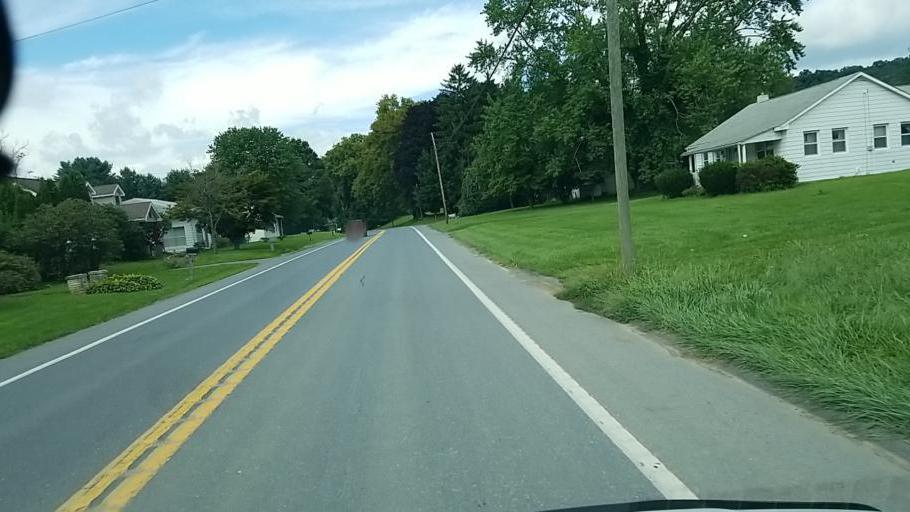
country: US
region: Pennsylvania
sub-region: Dauphin County
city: Matamoras
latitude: 40.4921
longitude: -76.9356
